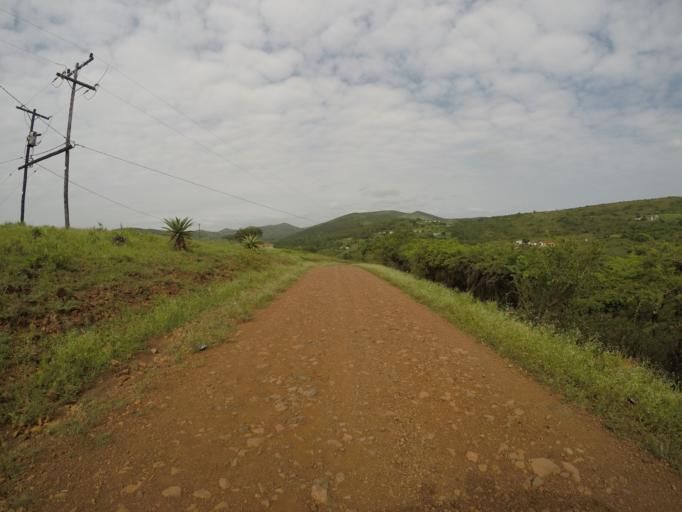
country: ZA
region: KwaZulu-Natal
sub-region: uThungulu District Municipality
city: Empangeni
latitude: -28.6249
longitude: 31.8976
